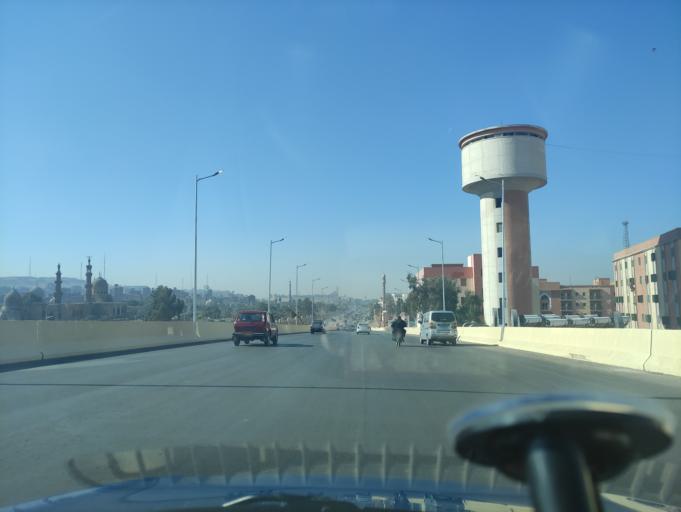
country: EG
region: Muhafazat al Qahirah
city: Cairo
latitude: 30.0555
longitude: 31.2795
